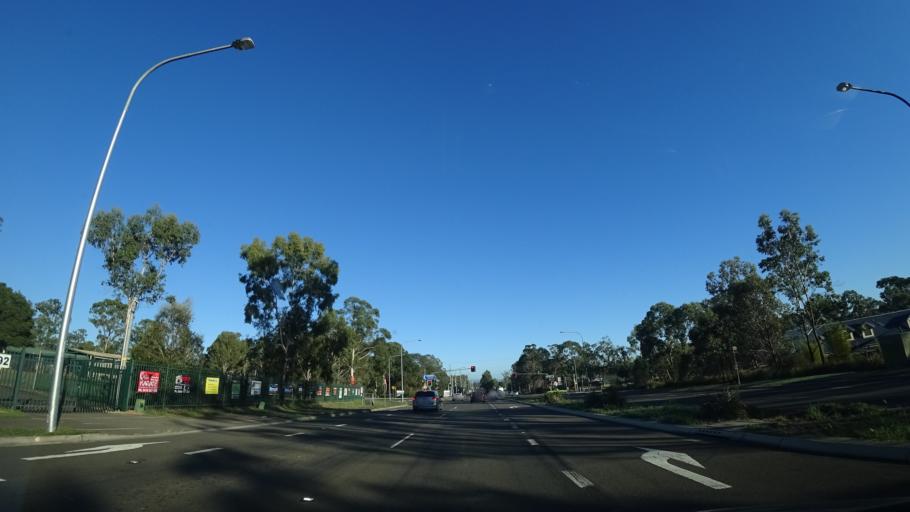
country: AU
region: New South Wales
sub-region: Blacktown
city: Riverstone
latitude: -33.6471
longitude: 150.8594
